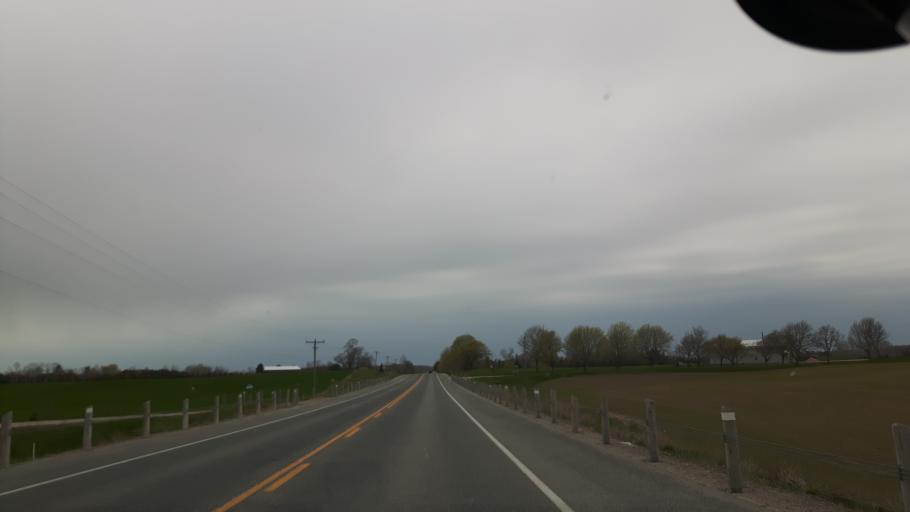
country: CA
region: Ontario
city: Bluewater
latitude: 43.6283
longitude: -81.5654
